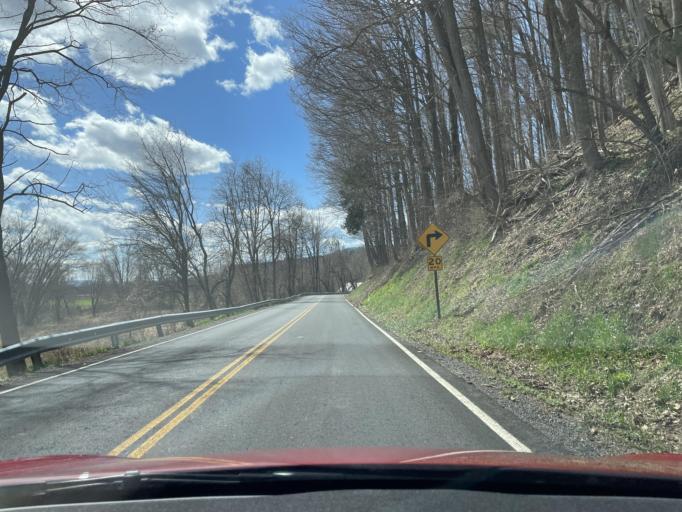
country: US
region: New York
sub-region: Ulster County
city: Hurley
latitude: 41.9405
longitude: -74.0624
